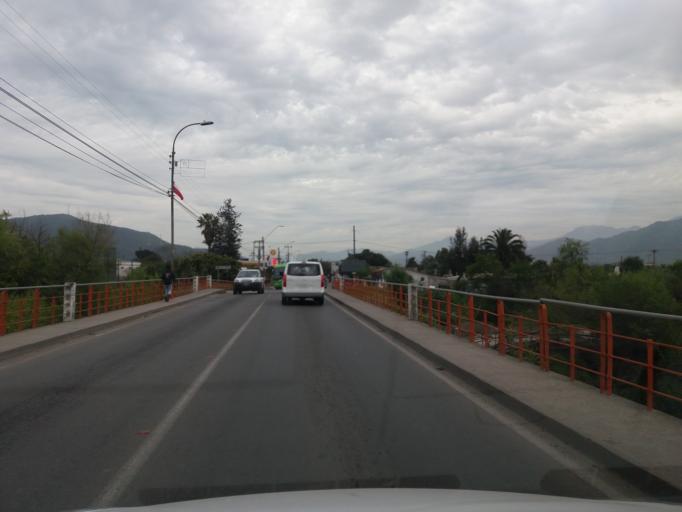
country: CL
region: Valparaiso
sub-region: Provincia de Quillota
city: Hacienda La Calera
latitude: -32.7791
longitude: -71.1913
